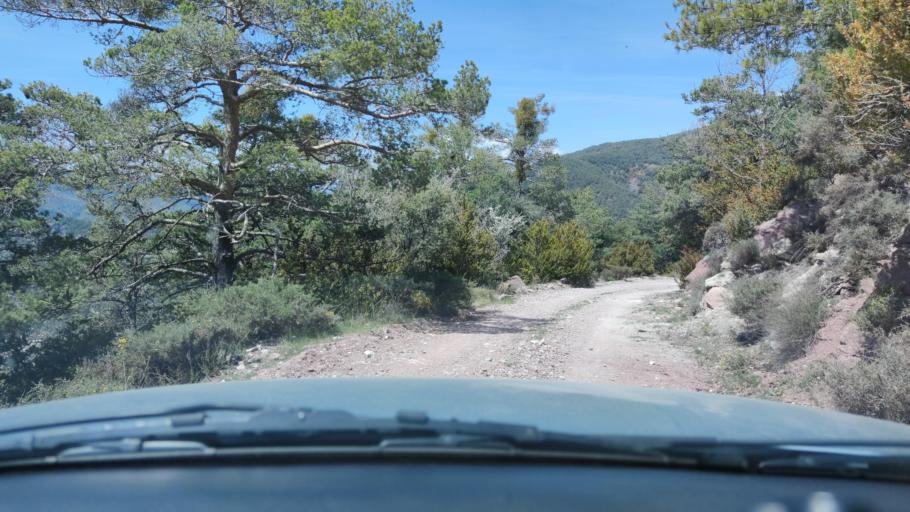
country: ES
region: Catalonia
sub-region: Provincia de Lleida
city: Sort
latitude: 42.3104
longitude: 1.1484
